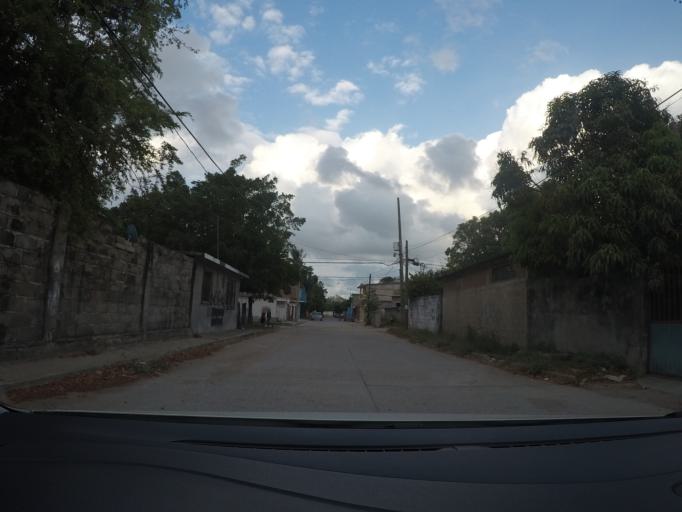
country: MX
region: Oaxaca
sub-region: Salina Cruz
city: Salina Cruz
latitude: 16.2088
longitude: -95.1984
